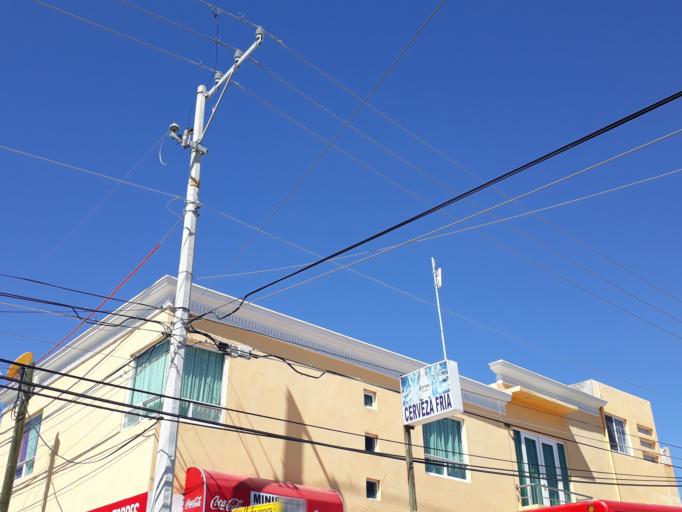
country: MX
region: Aguascalientes
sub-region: Aguascalientes
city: Aguascalientes
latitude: 21.8782
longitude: -102.2417
